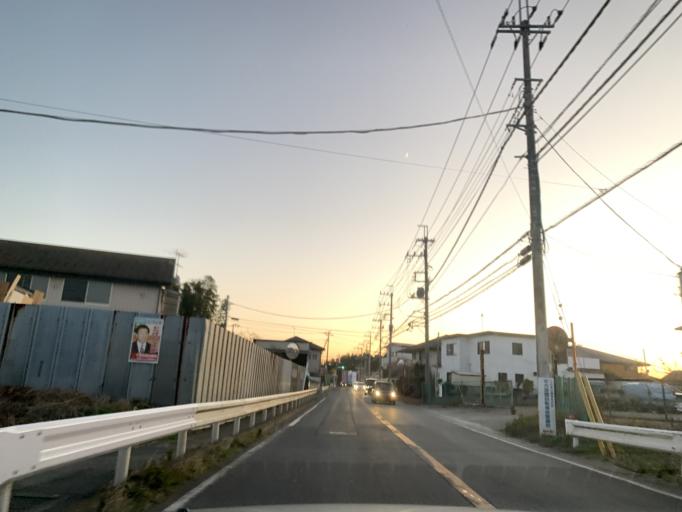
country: JP
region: Chiba
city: Nagareyama
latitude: 35.9056
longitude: 139.9024
